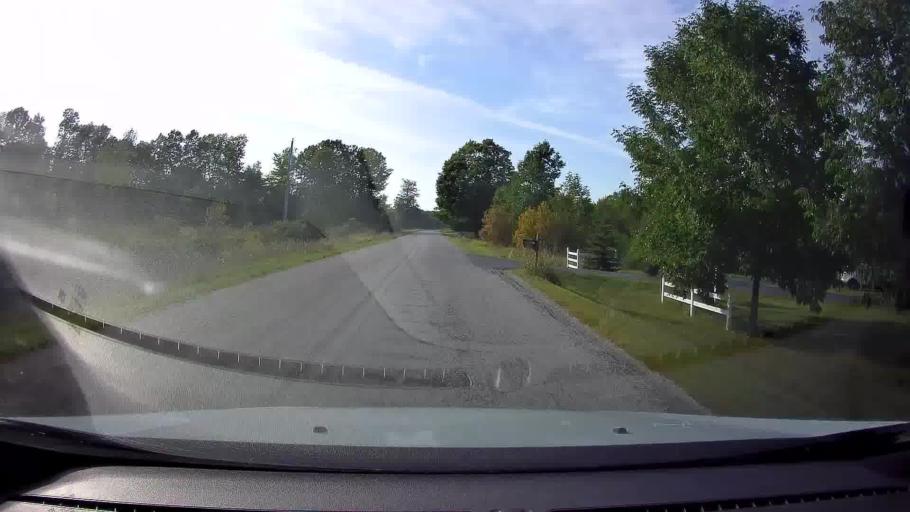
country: US
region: Wisconsin
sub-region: Door County
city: Sturgeon Bay
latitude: 45.1731
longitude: -87.1363
